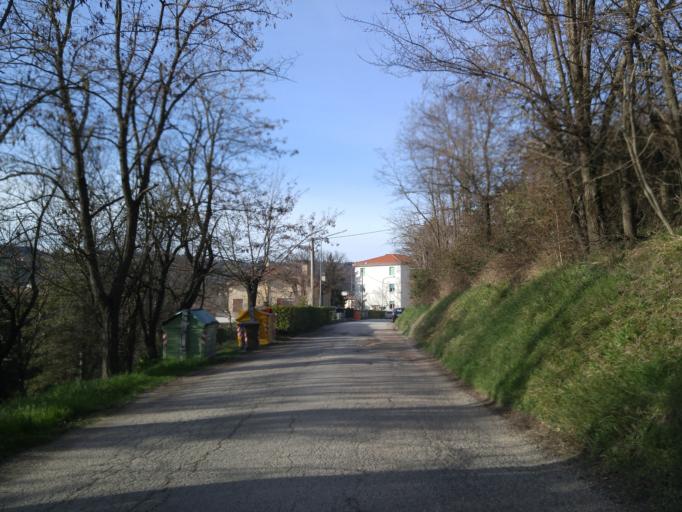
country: IT
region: The Marches
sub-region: Provincia di Pesaro e Urbino
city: Fermignano
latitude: 43.6774
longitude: 12.6480
